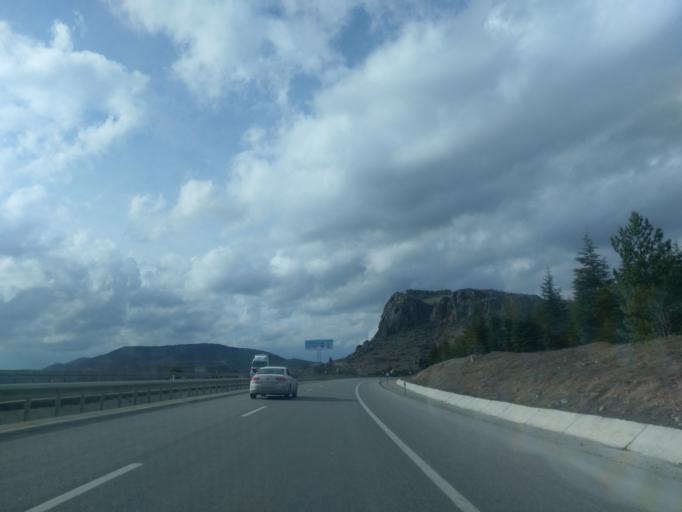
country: TR
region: Kuetahya
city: Sabuncu
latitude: 39.5714
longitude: 30.1057
